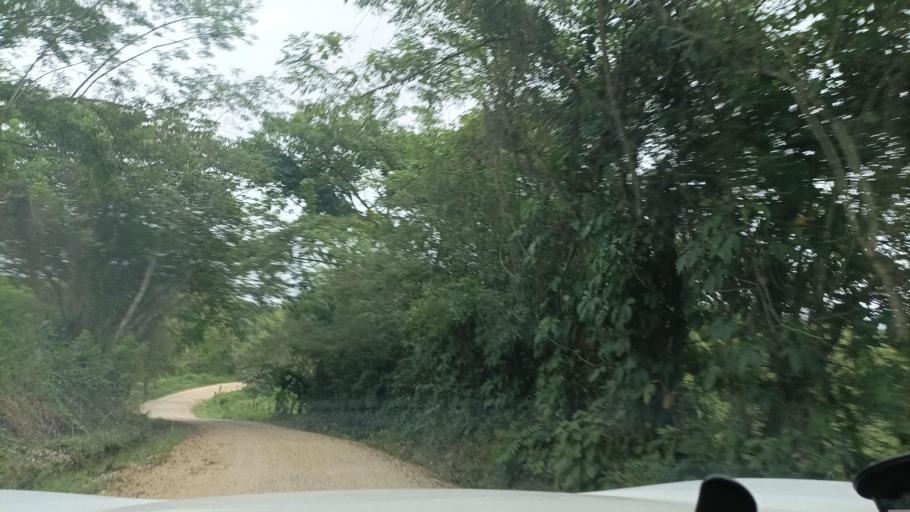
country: MX
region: Veracruz
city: Hidalgotitlan
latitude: 17.6095
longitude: -94.5235
